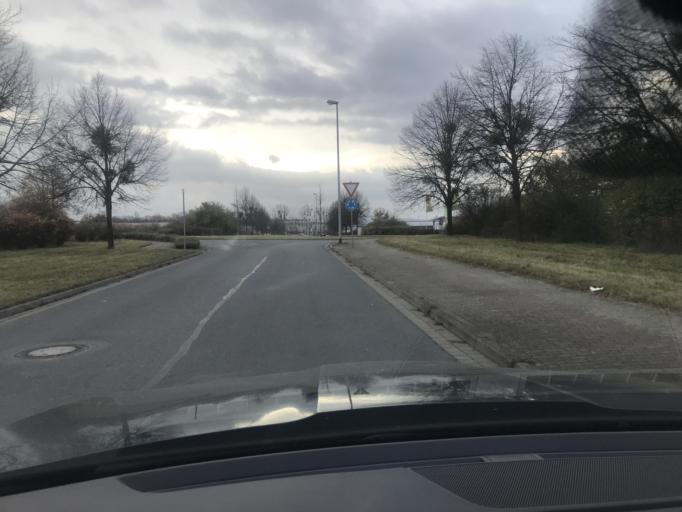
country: DE
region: Saxony-Anhalt
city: Quedlinburg
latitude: 51.7956
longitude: 11.1783
